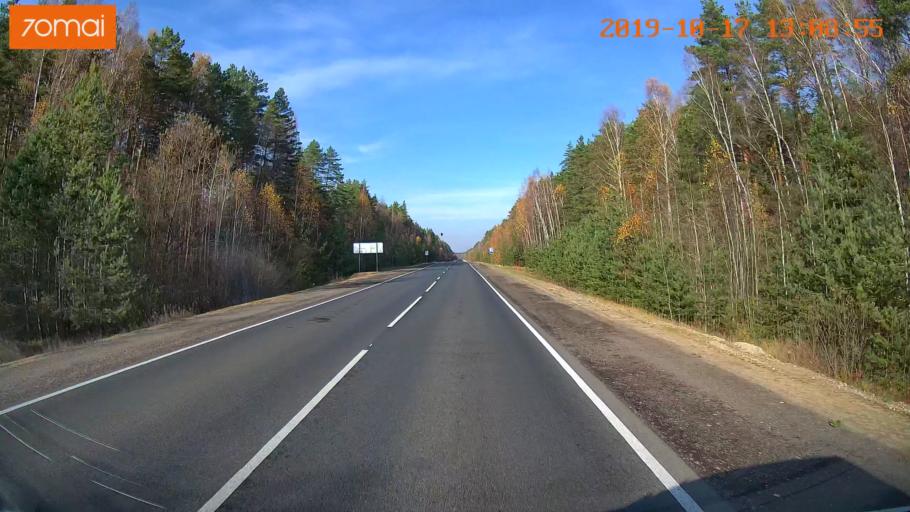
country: RU
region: Rjazan
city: Syntul
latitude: 54.9959
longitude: 41.2663
